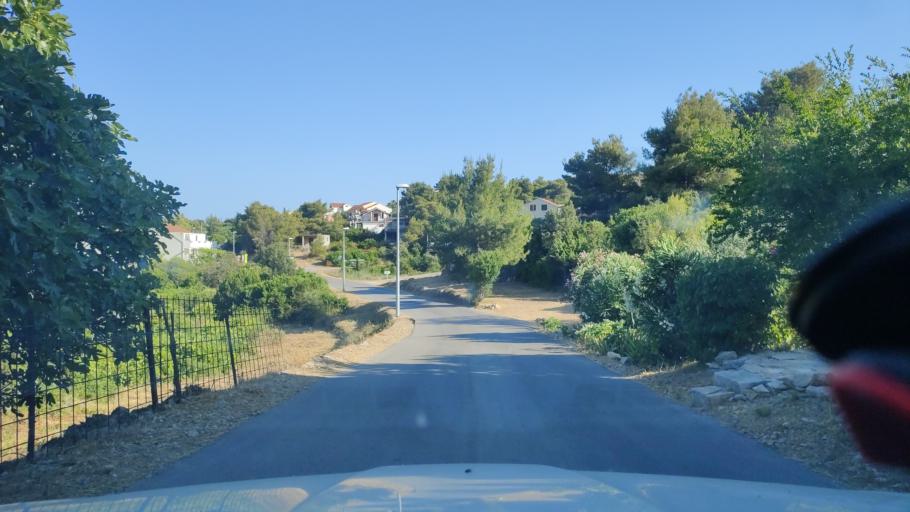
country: HR
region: Splitsko-Dalmatinska
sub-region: Grad Vis
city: Vis
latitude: 43.0284
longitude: 16.2052
